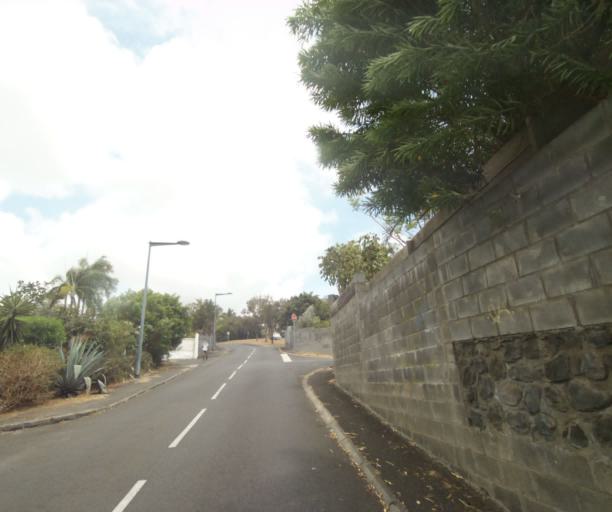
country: RE
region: Reunion
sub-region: Reunion
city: Saint-Paul
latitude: -21.0258
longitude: 55.2716
